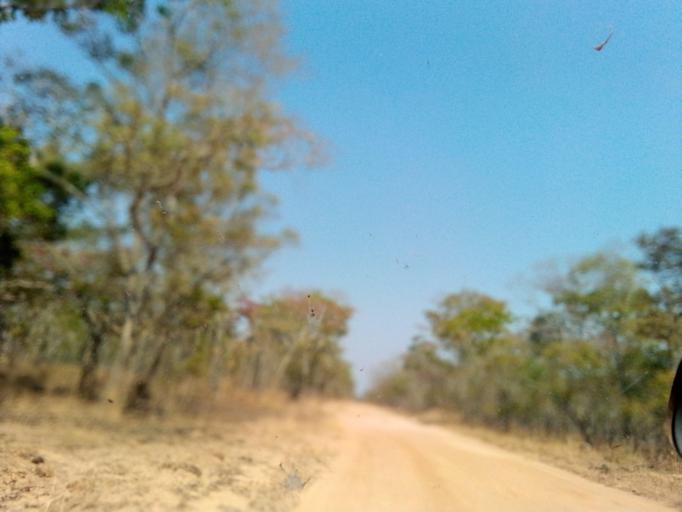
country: ZM
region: Northern
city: Mpika
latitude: -12.2419
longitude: 30.8306
